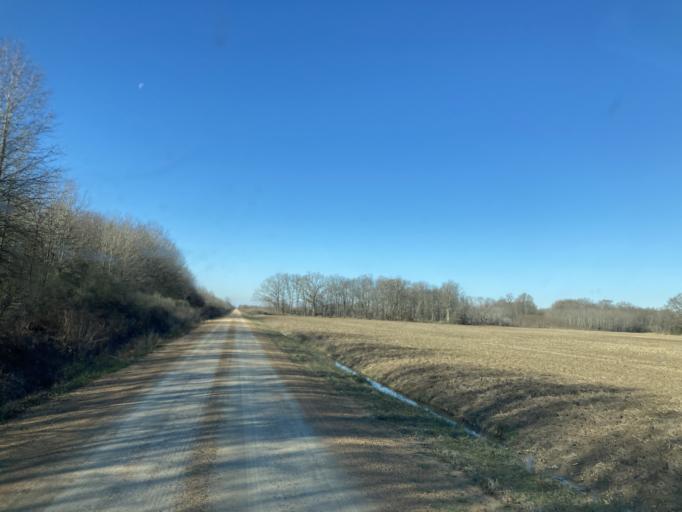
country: US
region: Mississippi
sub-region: Yazoo County
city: Yazoo City
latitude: 32.9519
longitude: -90.6115
